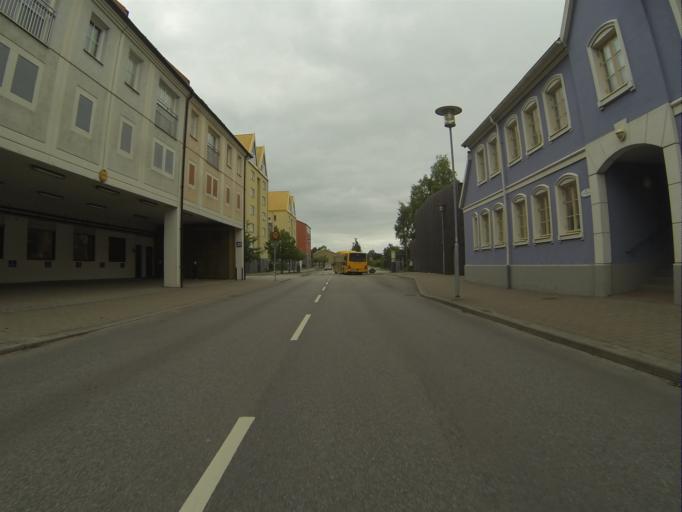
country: SE
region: Skane
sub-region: Staffanstorps Kommun
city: Staffanstorp
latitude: 55.6439
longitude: 13.2101
